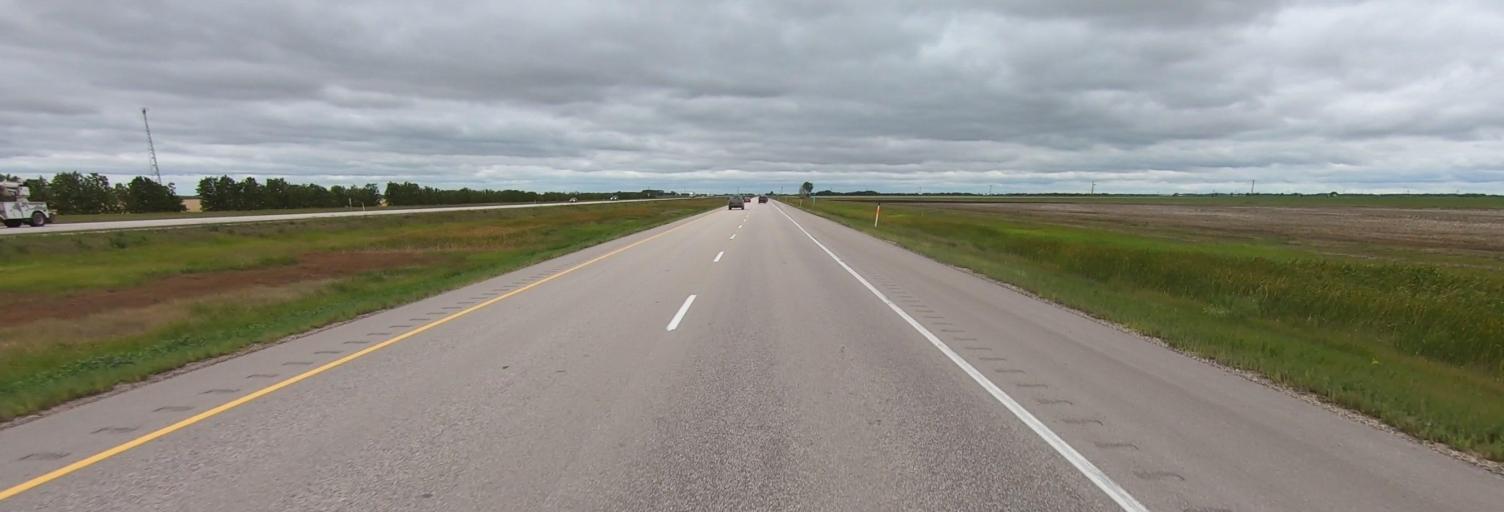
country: CA
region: Manitoba
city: Headingley
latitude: 49.9134
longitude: -97.7917
